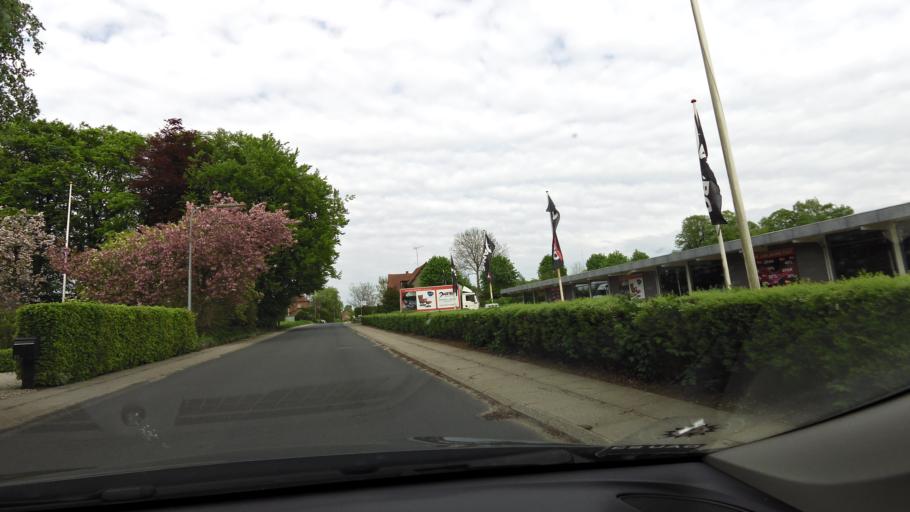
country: DK
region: South Denmark
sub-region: Svendborg Kommune
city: Thuro By
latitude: 55.1727
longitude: 10.7399
